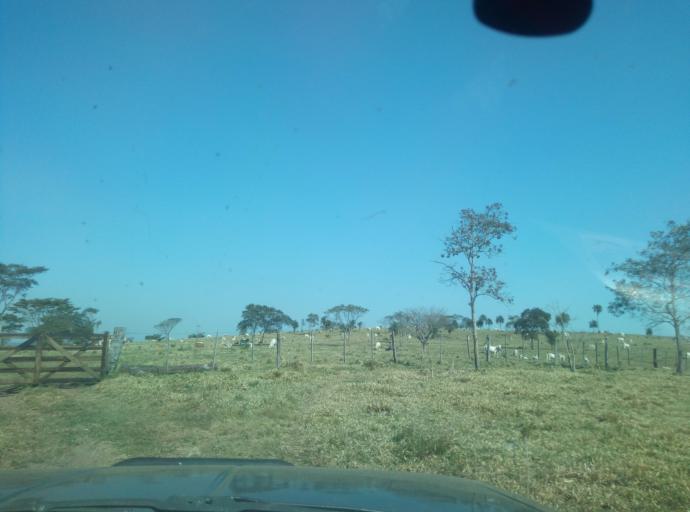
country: PY
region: Caaguazu
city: San Joaquin
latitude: -25.1746
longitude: -56.1114
